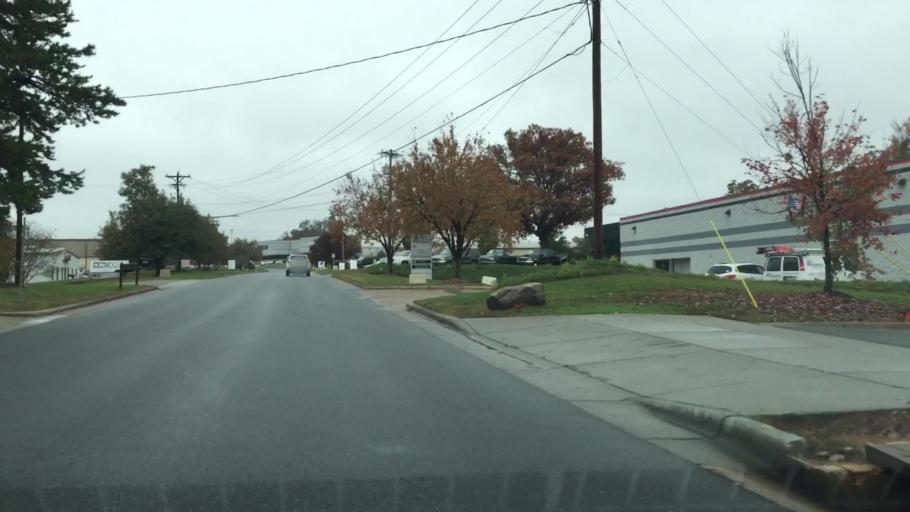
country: US
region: North Carolina
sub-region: Iredell County
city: Mooresville
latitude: 35.5852
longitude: -80.8604
